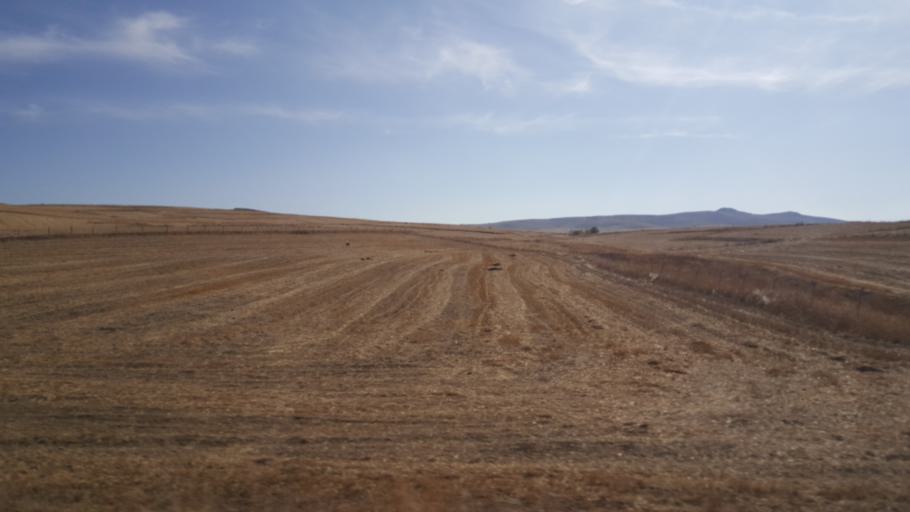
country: TR
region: Ankara
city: Yenice
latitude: 39.3677
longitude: 32.6952
